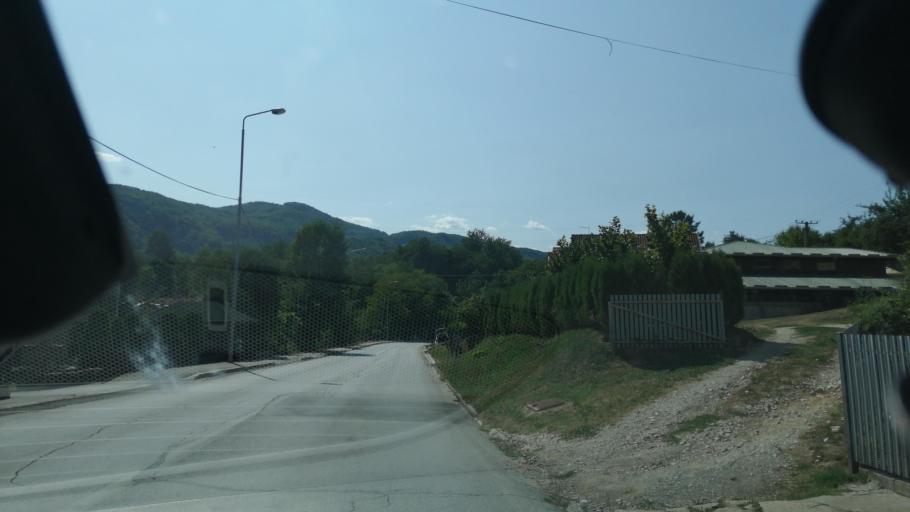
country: RS
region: Central Serbia
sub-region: Moravicki Okrug
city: Ivanjica
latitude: 43.5999
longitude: 20.2279
